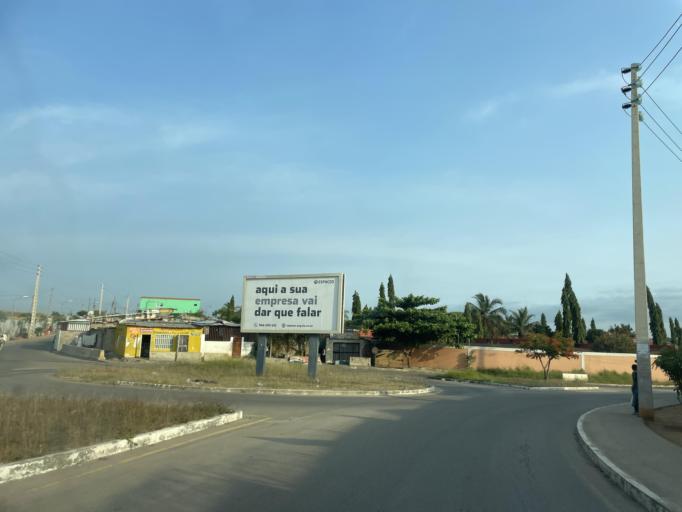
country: AO
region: Luanda
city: Luanda
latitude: -8.9178
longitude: 13.2051
